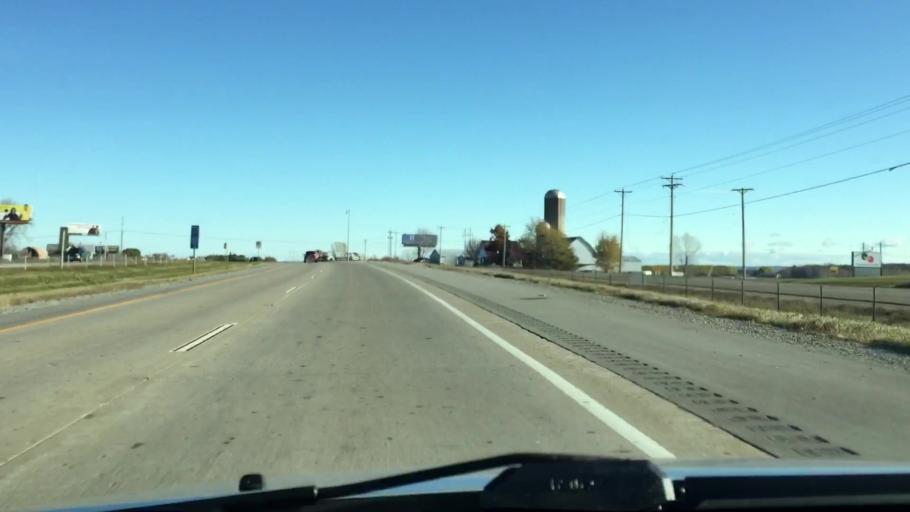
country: US
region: Wisconsin
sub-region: Brown County
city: Wrightstown
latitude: 44.3215
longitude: -88.2177
